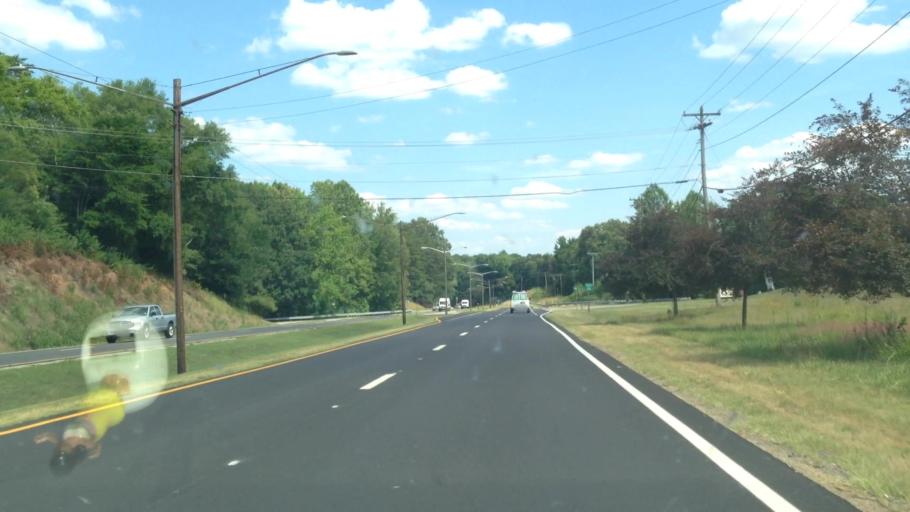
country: US
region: Virginia
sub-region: City of Danville
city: Danville
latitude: 36.5831
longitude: -79.4438
